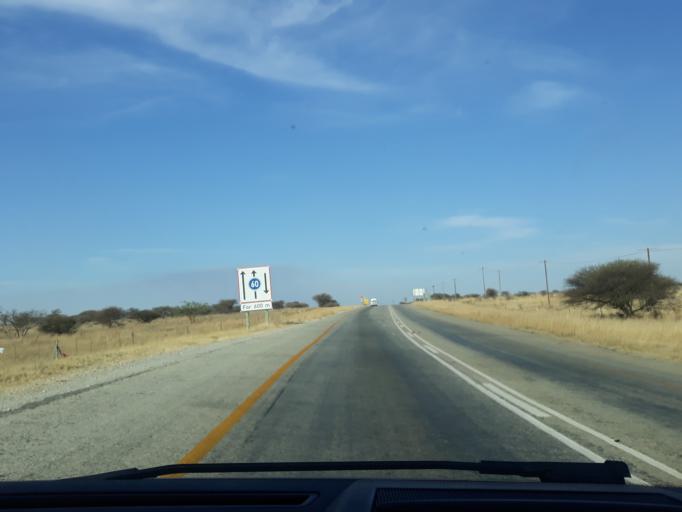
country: ZA
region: Limpopo
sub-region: Capricorn District Municipality
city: Polokwane
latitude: -23.9477
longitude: 29.4057
